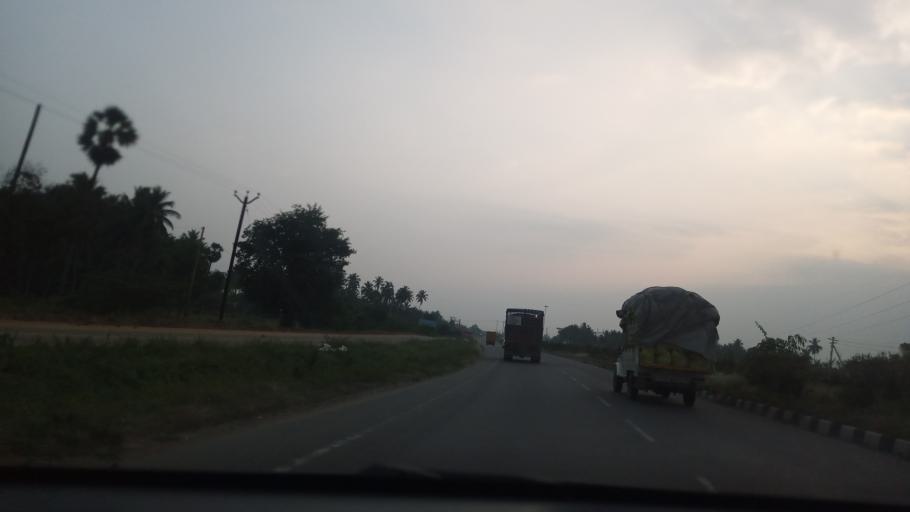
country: IN
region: Tamil Nadu
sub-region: Erode
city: Perundurai
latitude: 11.3060
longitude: 77.6041
